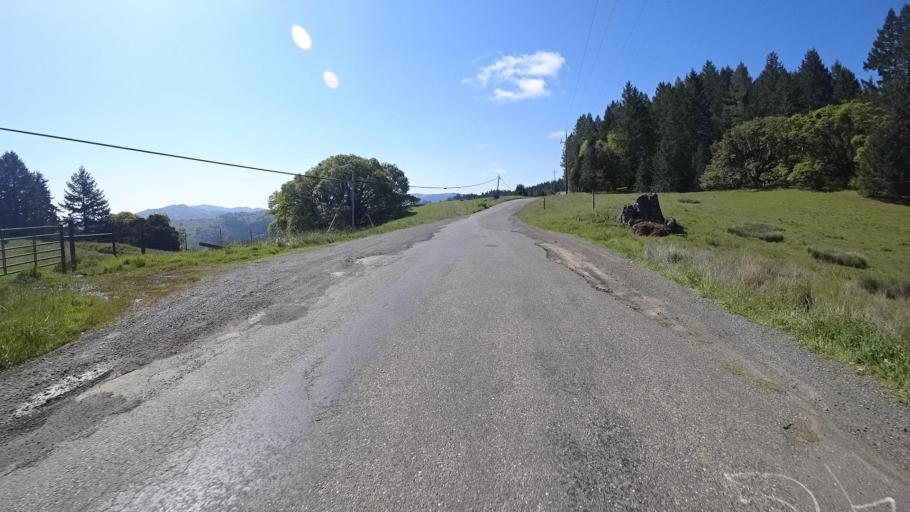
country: US
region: California
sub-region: Humboldt County
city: Redway
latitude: 40.0553
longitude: -123.6394
